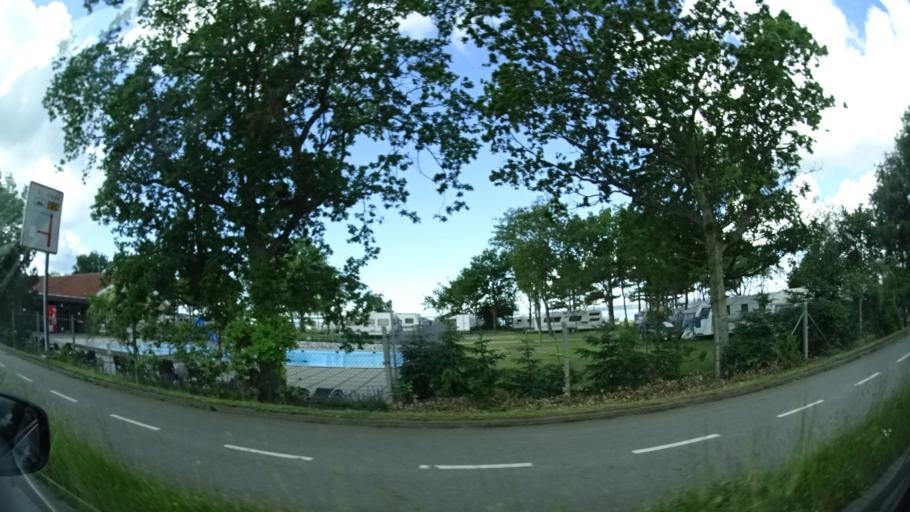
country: DK
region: Central Jutland
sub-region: Syddjurs Kommune
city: Ebeltoft
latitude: 56.2134
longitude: 10.6771
